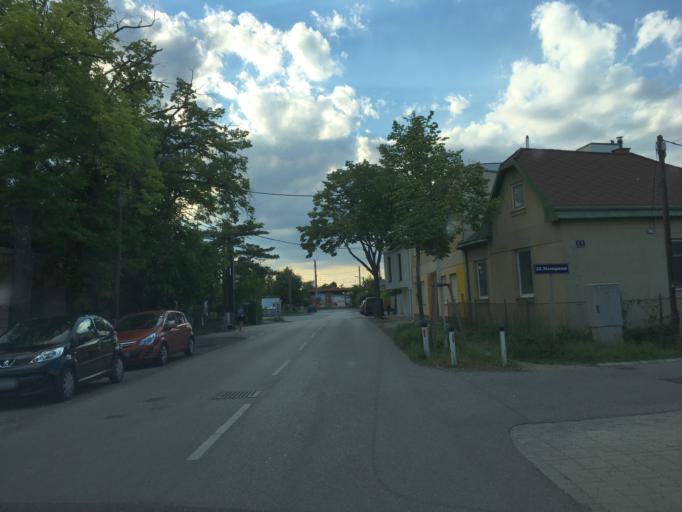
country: AT
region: Lower Austria
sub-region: Politischer Bezirk Wien-Umgebung
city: Gerasdorf bei Wien
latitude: 48.2843
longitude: 16.4858
